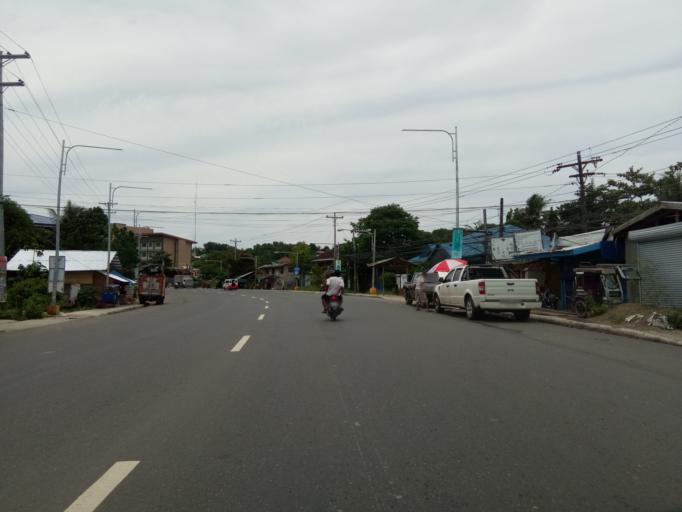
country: PH
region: Caraga
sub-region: Province of Surigao del Norte
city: Surigao
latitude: 9.7736
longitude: 125.4838
